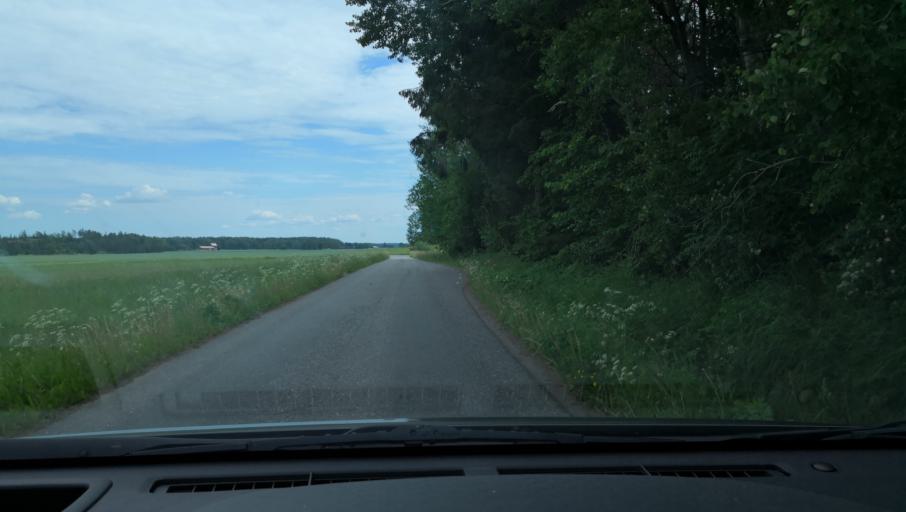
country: SE
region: Uppsala
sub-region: Enkopings Kommun
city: Orsundsbro
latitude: 59.6969
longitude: 17.4047
